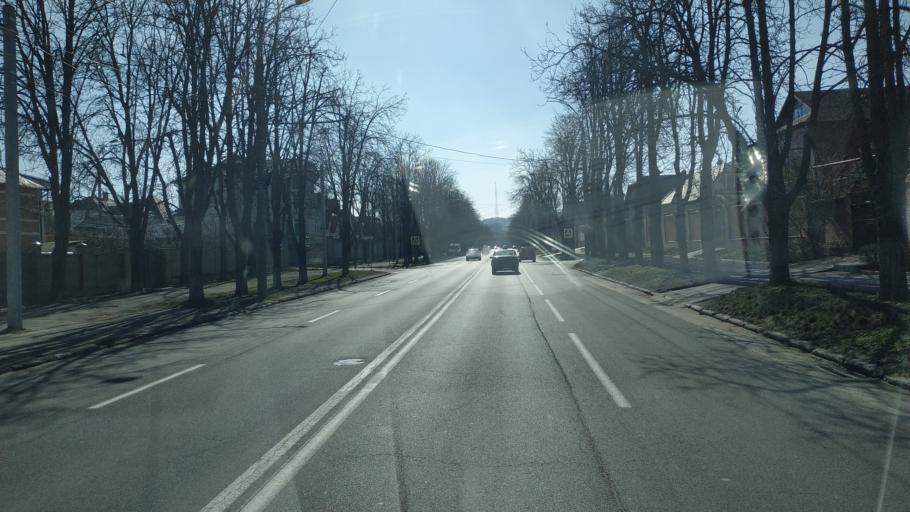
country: MD
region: Chisinau
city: Chisinau
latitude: 47.0268
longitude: 28.8026
